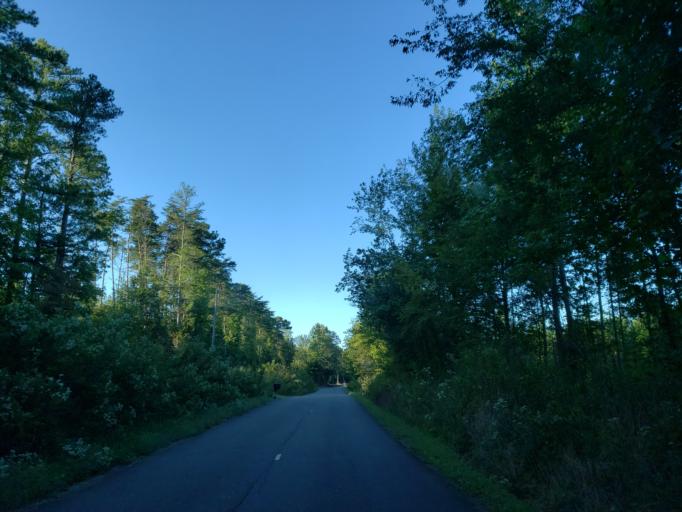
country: US
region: Georgia
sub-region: Bartow County
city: Rydal
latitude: 34.3117
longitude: -84.7325
